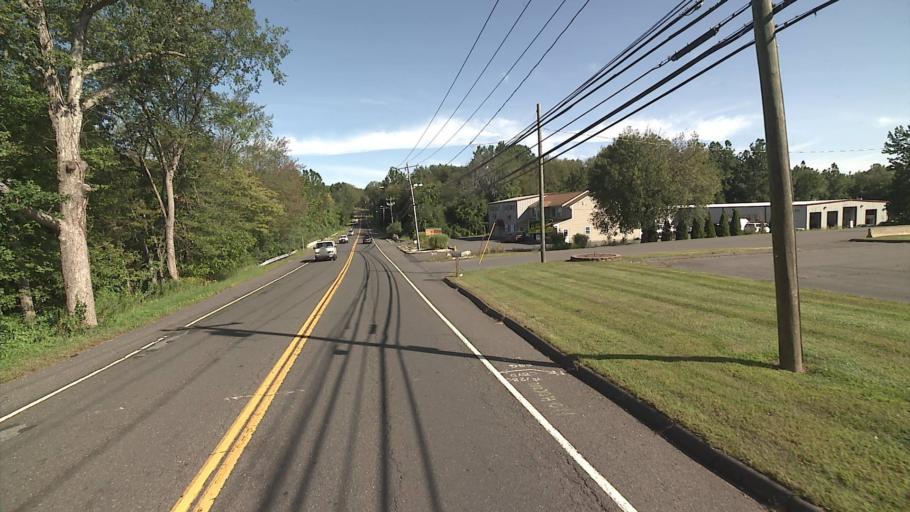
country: US
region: Connecticut
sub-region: New Haven County
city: Cheshire Village
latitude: 41.5261
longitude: -72.9323
